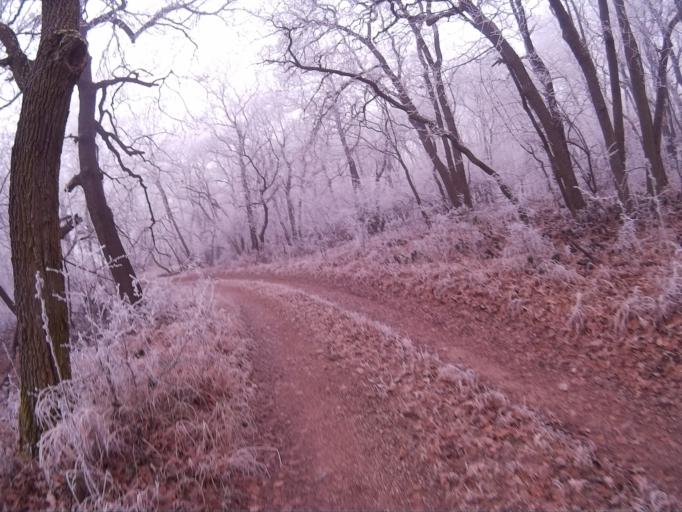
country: HU
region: Komarom-Esztergom
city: Oroszlany
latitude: 47.3933
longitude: 18.3317
